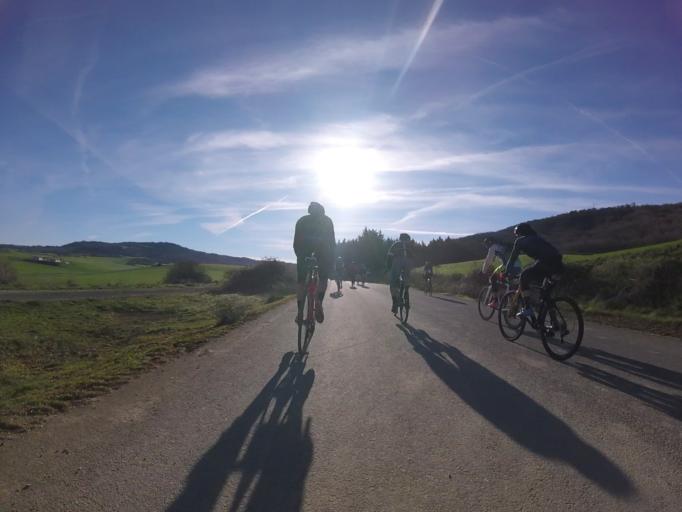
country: ES
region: Navarre
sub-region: Provincia de Navarra
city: Villatuerta
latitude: 42.6562
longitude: -1.9824
